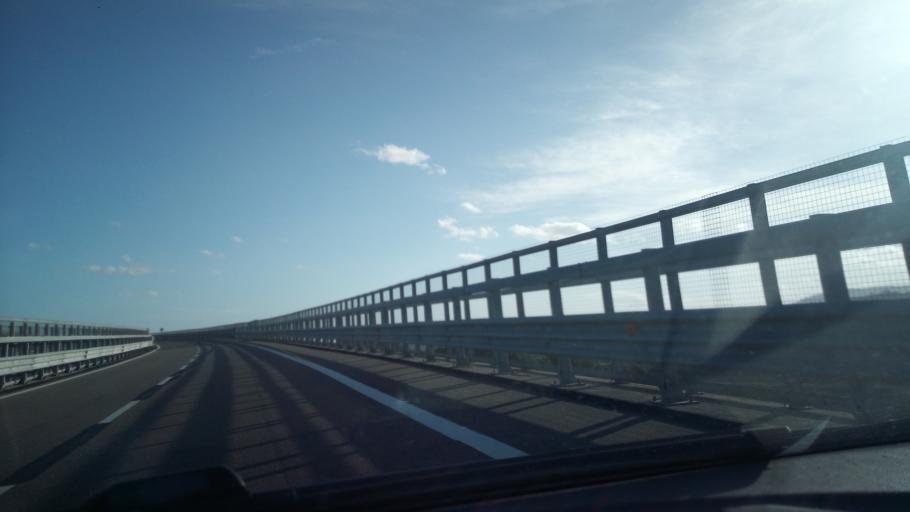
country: IT
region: Calabria
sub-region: Provincia di Catanzaro
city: Roccelletta
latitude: 38.8319
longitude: 16.5921
